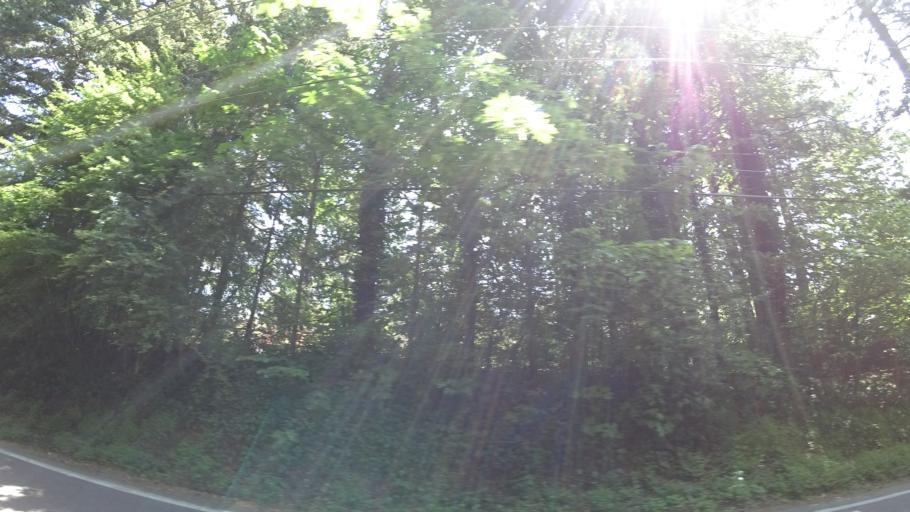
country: US
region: Oregon
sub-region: Washington County
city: Metzger
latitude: 45.4410
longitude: -122.7129
